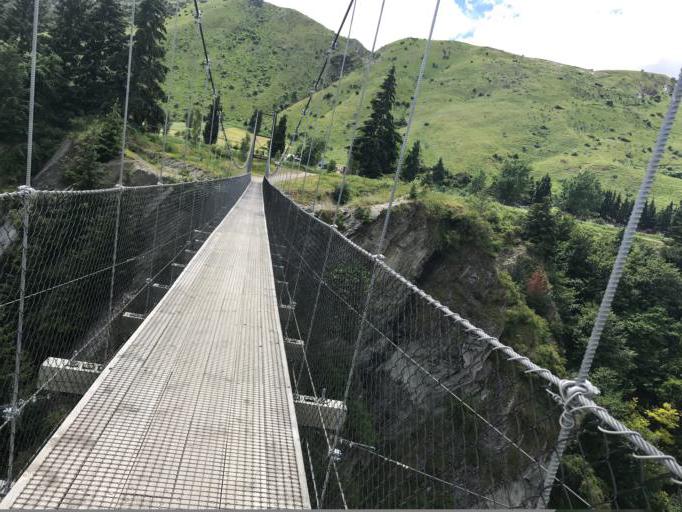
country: NZ
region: Otago
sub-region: Queenstown-Lakes District
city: Arrowtown
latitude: -45.0015
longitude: 168.8733
